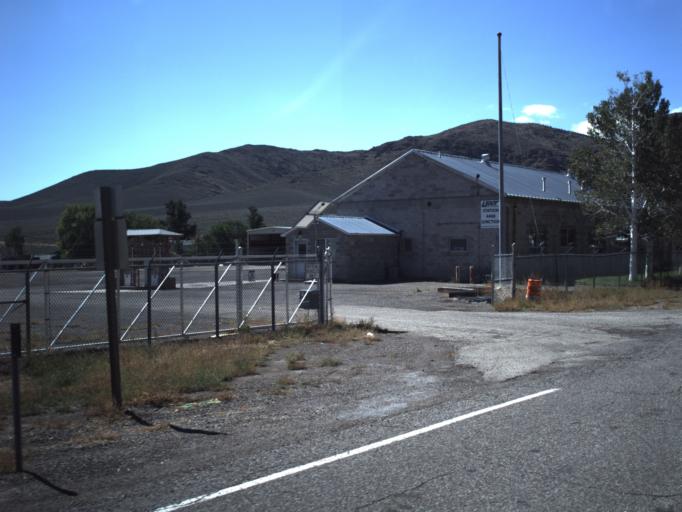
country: US
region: Utah
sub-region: Piute County
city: Junction
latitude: 38.2369
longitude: -112.2238
